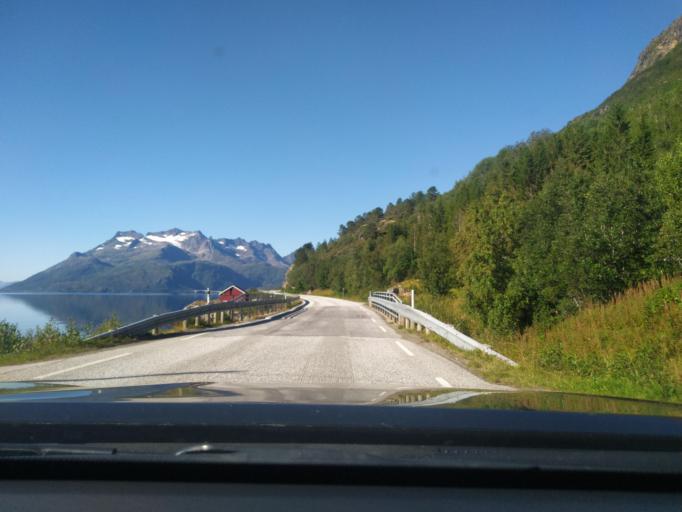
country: NO
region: Troms
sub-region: Dyroy
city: Brostadbotn
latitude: 68.9213
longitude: 17.6227
